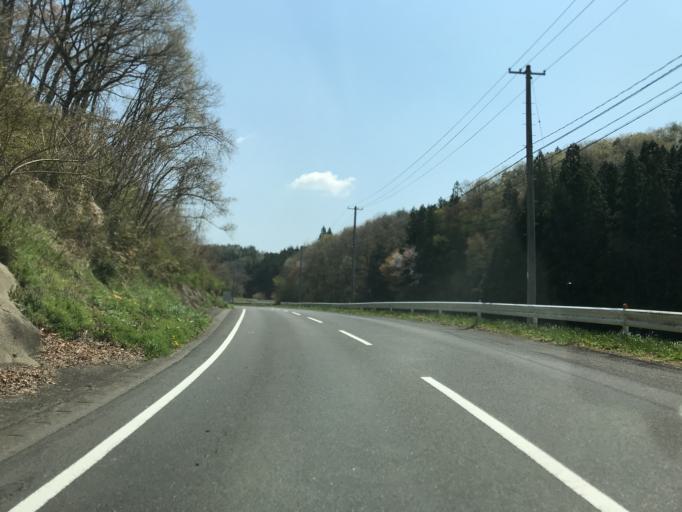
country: JP
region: Fukushima
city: Ishikawa
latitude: 37.0669
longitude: 140.4365
